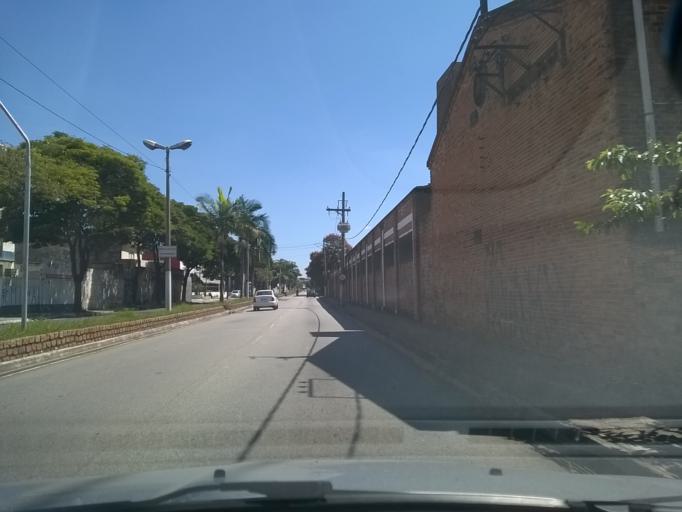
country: BR
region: Sao Paulo
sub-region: Jundiai
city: Jundiai
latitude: -23.1804
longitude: -46.8844
